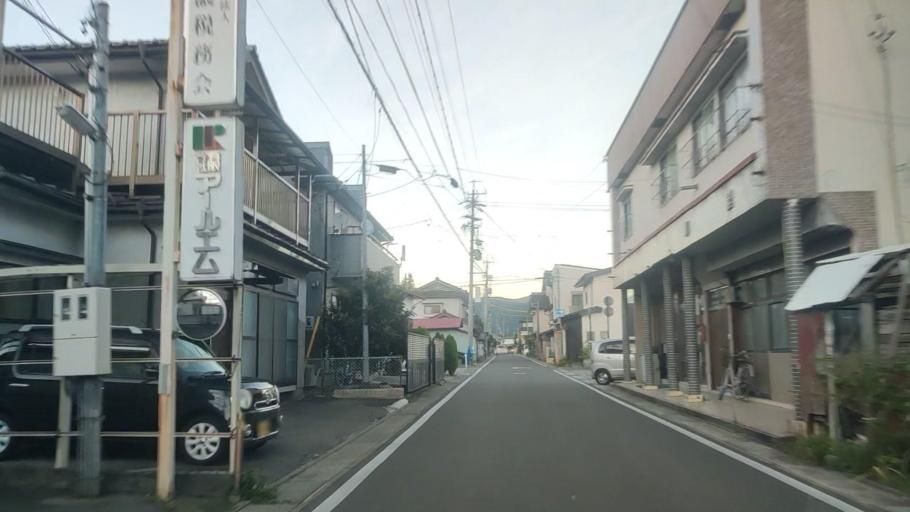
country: JP
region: Nagano
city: Okaya
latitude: 36.0698
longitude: 138.0524
